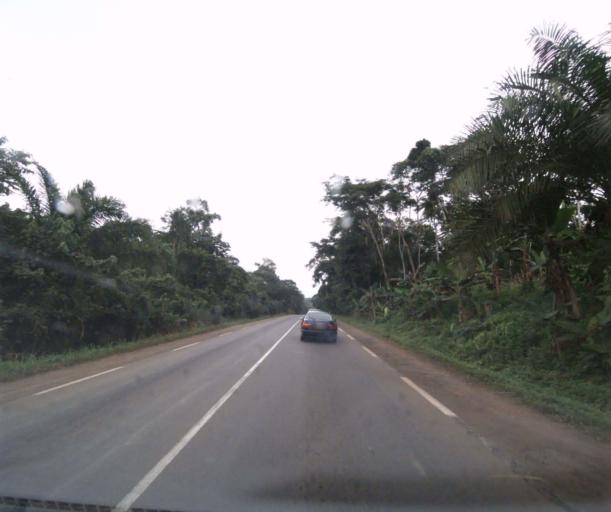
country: CM
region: Centre
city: Mbankomo
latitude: 3.7837
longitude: 11.2552
